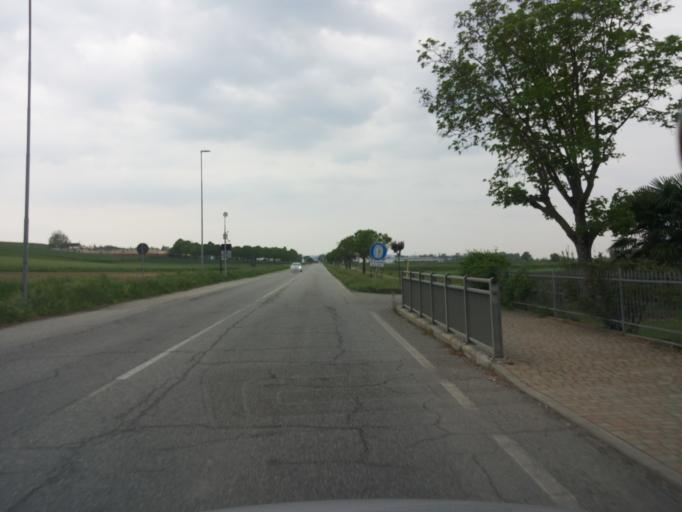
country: IT
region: Piedmont
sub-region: Provincia di Alessandria
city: Occimiano
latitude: 45.0631
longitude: 8.5043
